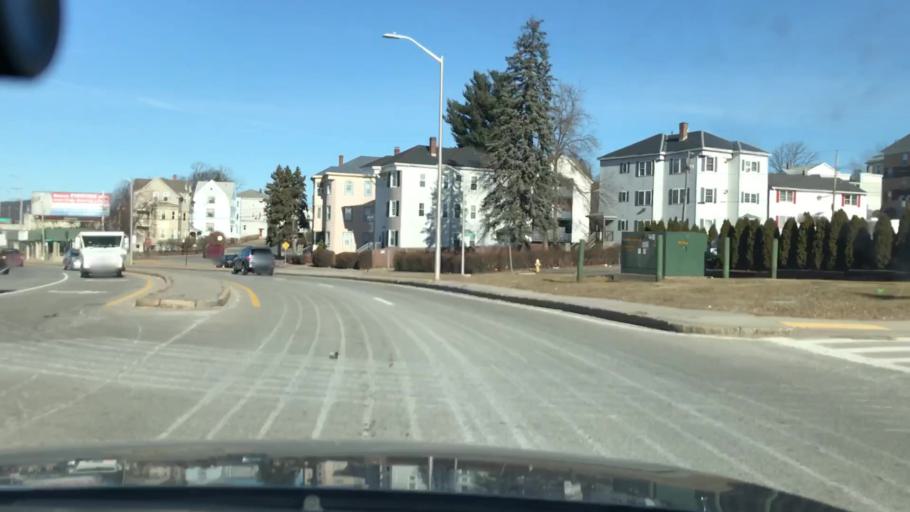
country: US
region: Massachusetts
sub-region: Worcester County
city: Worcester
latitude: 42.3011
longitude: -71.8000
